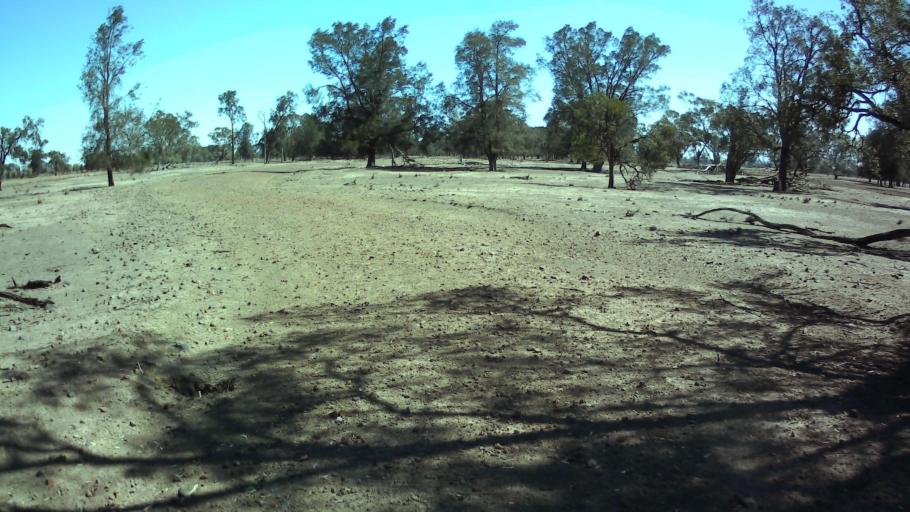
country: AU
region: New South Wales
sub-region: Bland
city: West Wyalong
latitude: -33.7637
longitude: 147.6582
